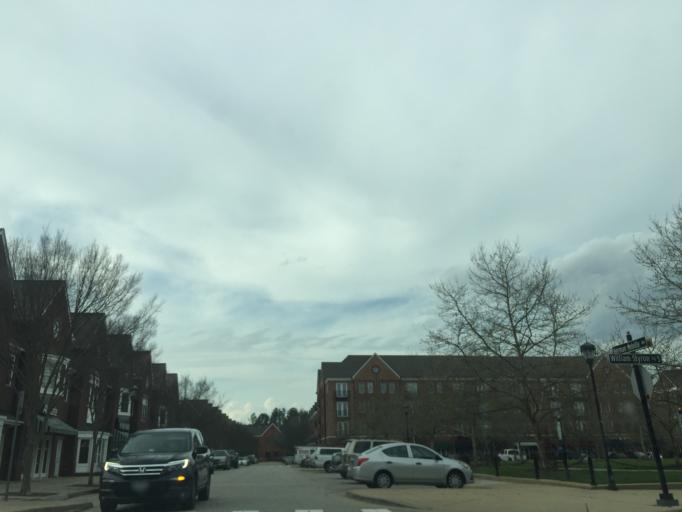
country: US
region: Virginia
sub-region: City of Newport News
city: Newport News
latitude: 37.0831
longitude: -76.4882
